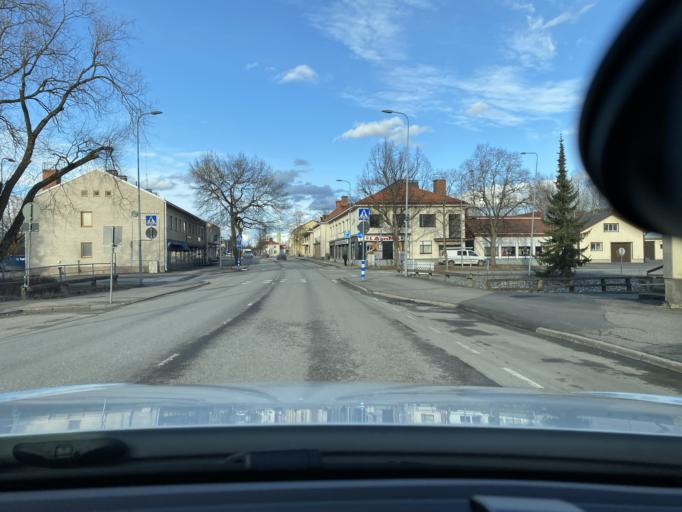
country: FI
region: Satakunta
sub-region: Pori
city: Huittinen
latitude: 61.1748
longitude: 22.6953
